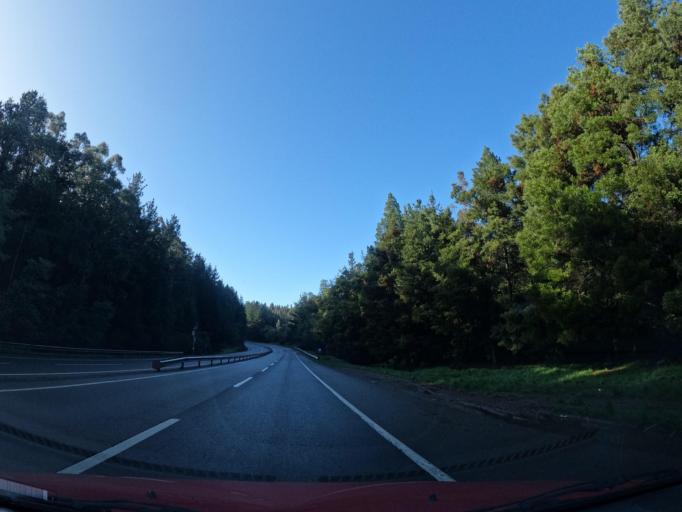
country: CL
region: Biobio
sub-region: Provincia de Concepcion
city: Penco
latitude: -36.7604
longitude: -72.9588
